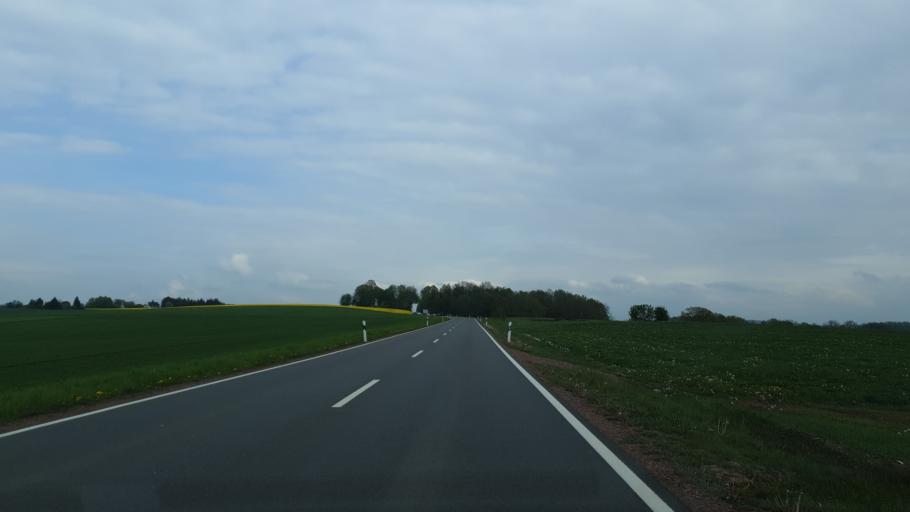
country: DE
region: Saxony
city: Gersdorf
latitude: 50.7498
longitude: 12.7286
